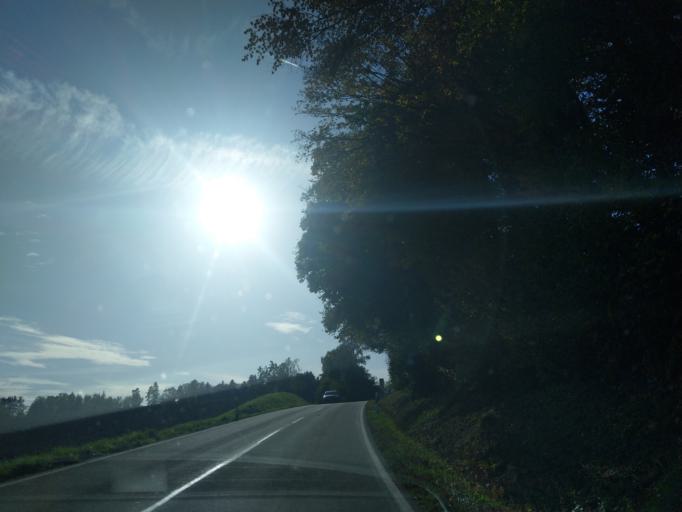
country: DE
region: Bavaria
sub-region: Lower Bavaria
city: Bernried
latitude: 48.9150
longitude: 12.8735
